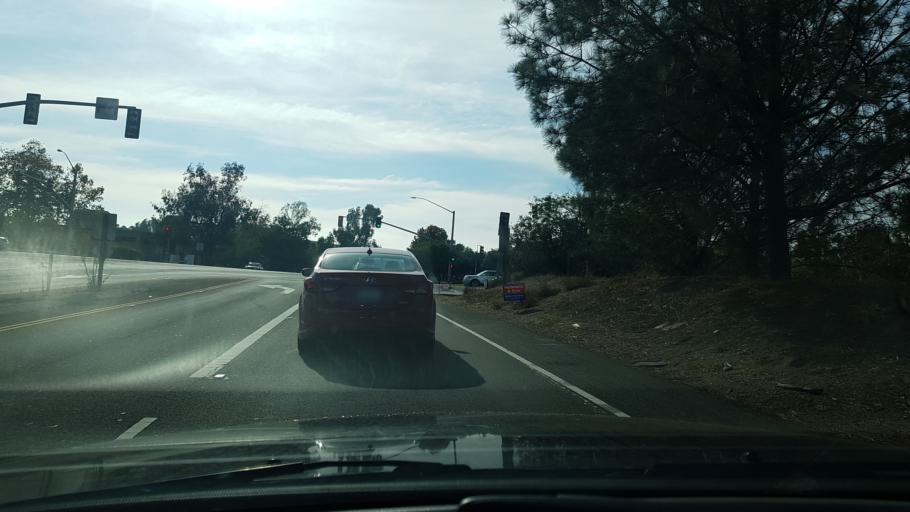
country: US
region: California
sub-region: San Diego County
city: Del Mar
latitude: 32.9386
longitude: -117.2291
